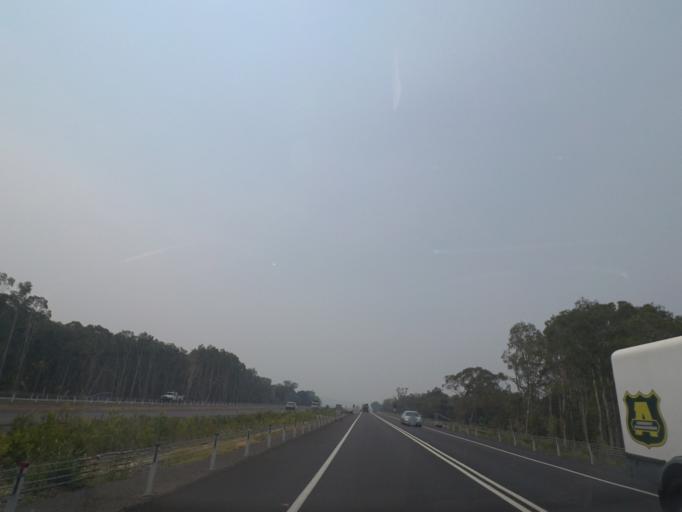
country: AU
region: New South Wales
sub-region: Ballina
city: Ballina
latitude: -28.9120
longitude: 153.4787
